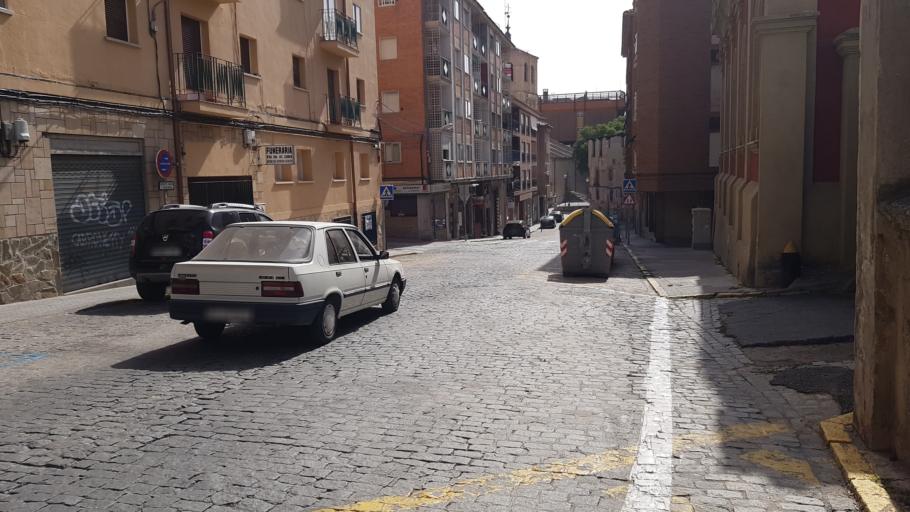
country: ES
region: Castille and Leon
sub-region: Provincia de Segovia
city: Segovia
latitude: 40.9445
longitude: -4.1143
